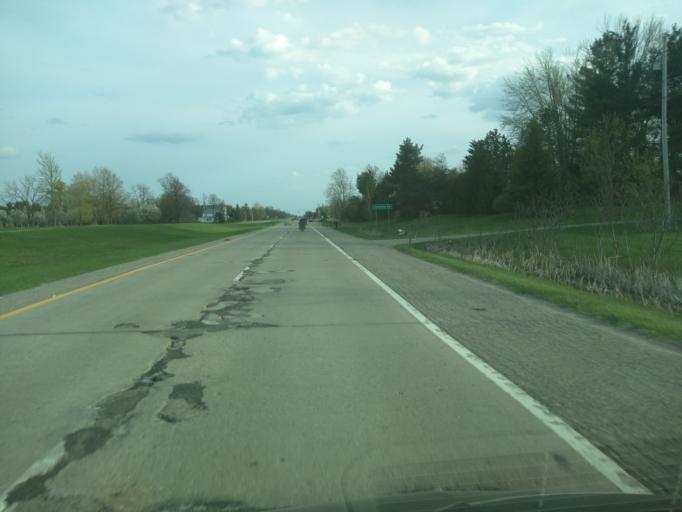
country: US
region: Michigan
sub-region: Eaton County
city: Dimondale
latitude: 42.5847
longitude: -84.6223
